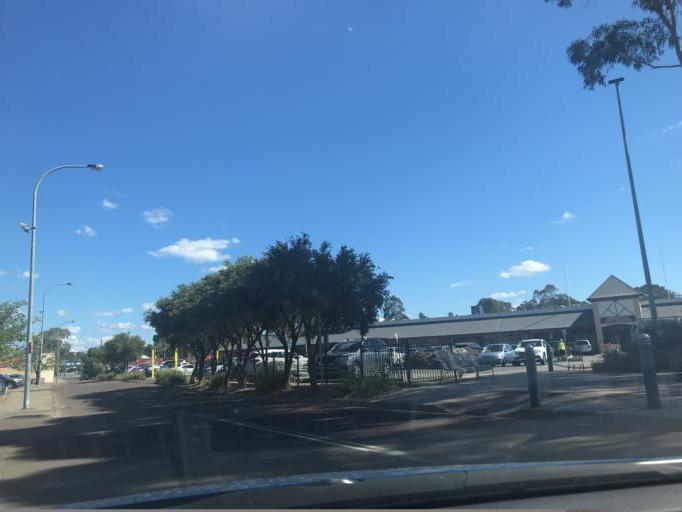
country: AU
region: New South Wales
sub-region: Cessnock
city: Cessnock
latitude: -32.8354
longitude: 151.3552
